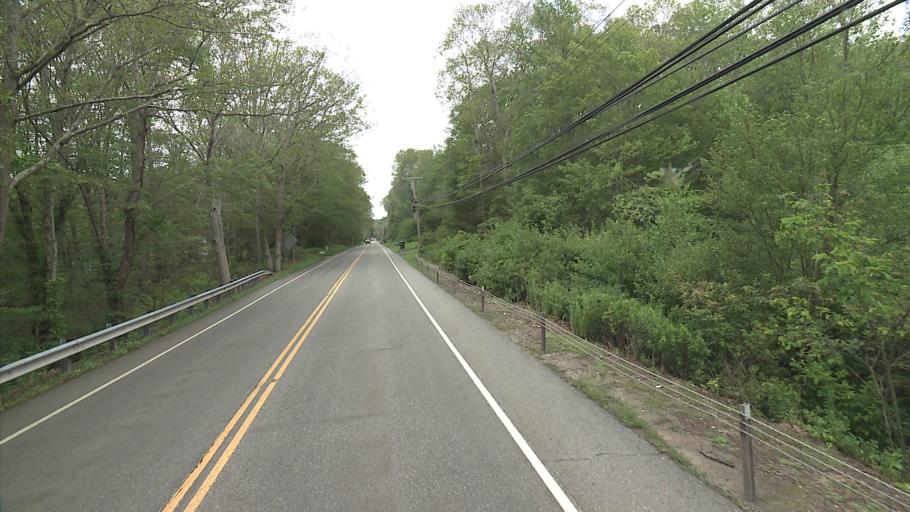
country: US
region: Connecticut
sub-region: New Haven County
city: Guilford
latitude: 41.3509
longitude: -72.6663
